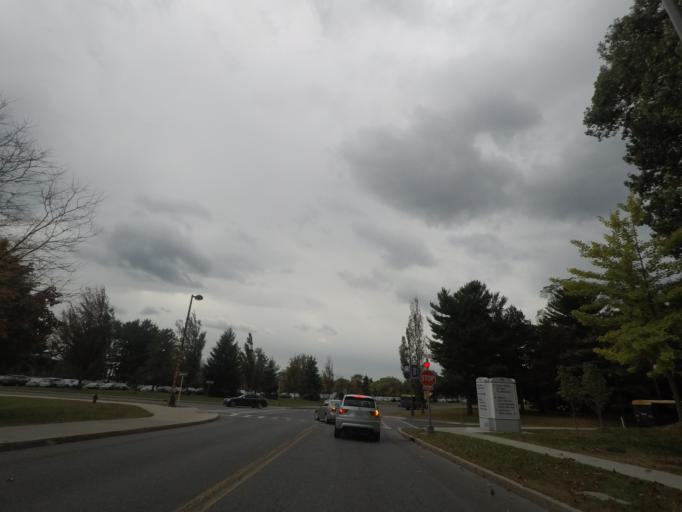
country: US
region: New York
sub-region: Albany County
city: McKownville
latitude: 42.6880
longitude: -73.8287
